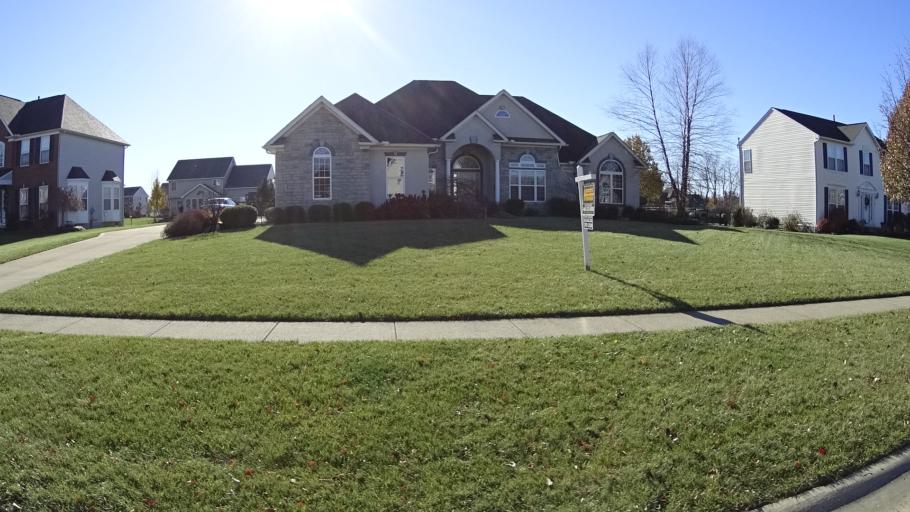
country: US
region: Ohio
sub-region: Lorain County
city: Avon
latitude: 41.4230
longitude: -82.0581
